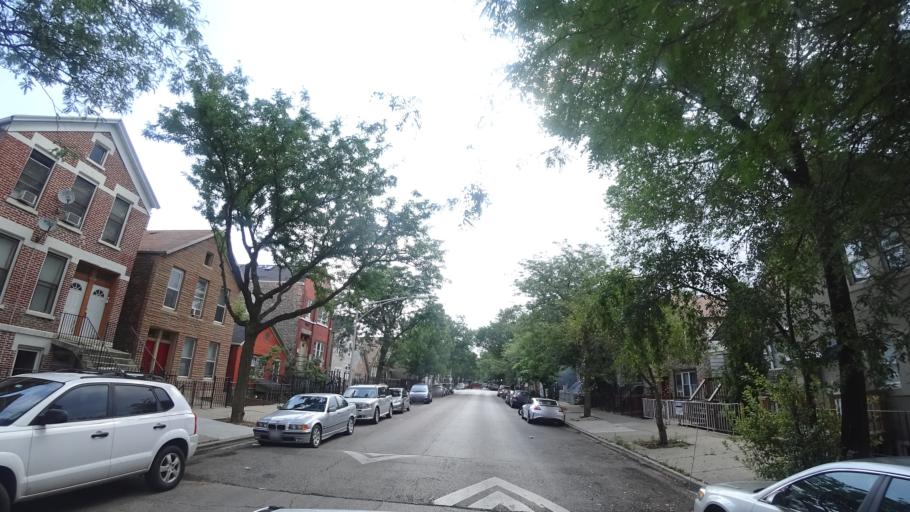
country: US
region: Illinois
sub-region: Cook County
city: Chicago
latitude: 41.8549
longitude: -87.6793
